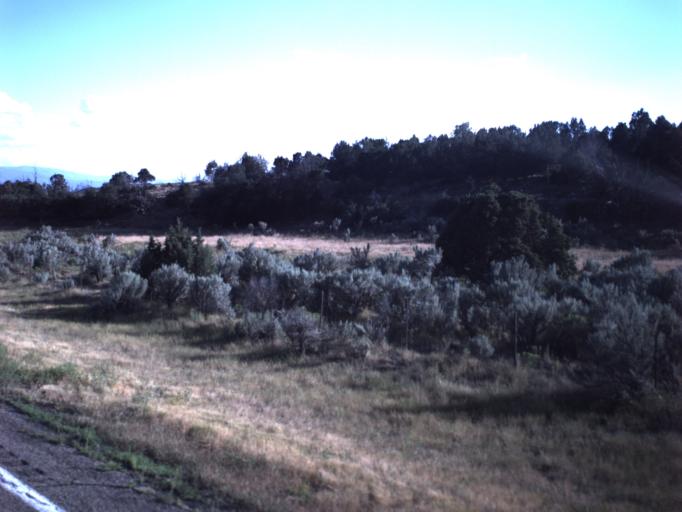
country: US
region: Utah
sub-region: Sanpete County
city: Fairview
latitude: 39.6592
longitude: -111.4508
